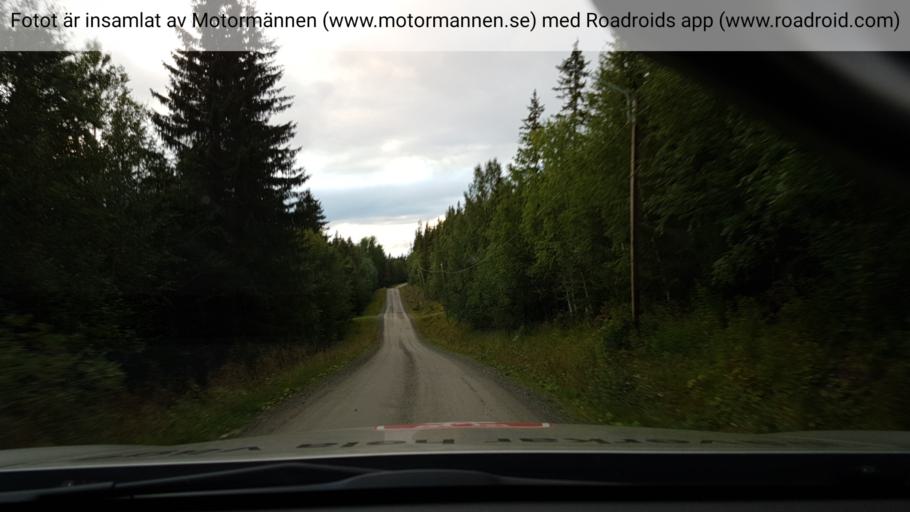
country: SE
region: Vaesterbotten
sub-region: Vilhelmina Kommun
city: Sjoberg
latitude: 65.6073
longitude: 15.2696
